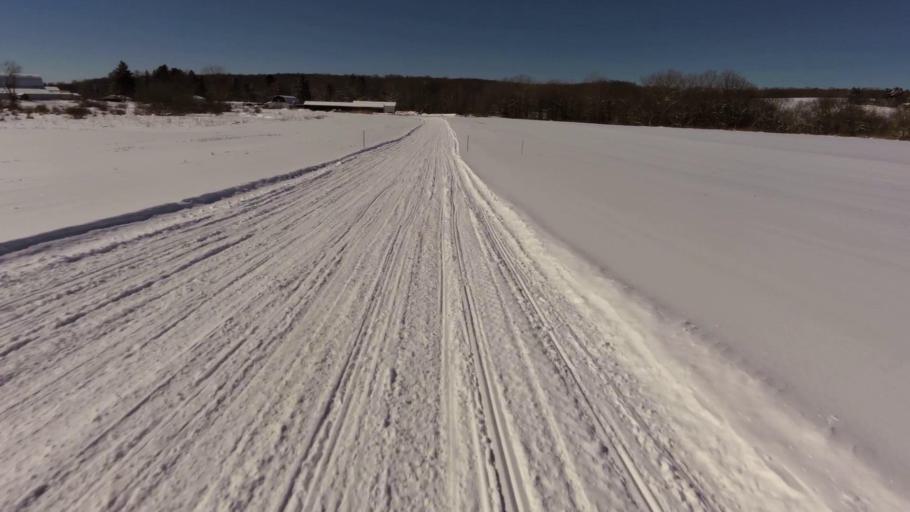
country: US
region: New York
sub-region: Chautauqua County
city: Mayville
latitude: 42.2477
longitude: -79.4340
